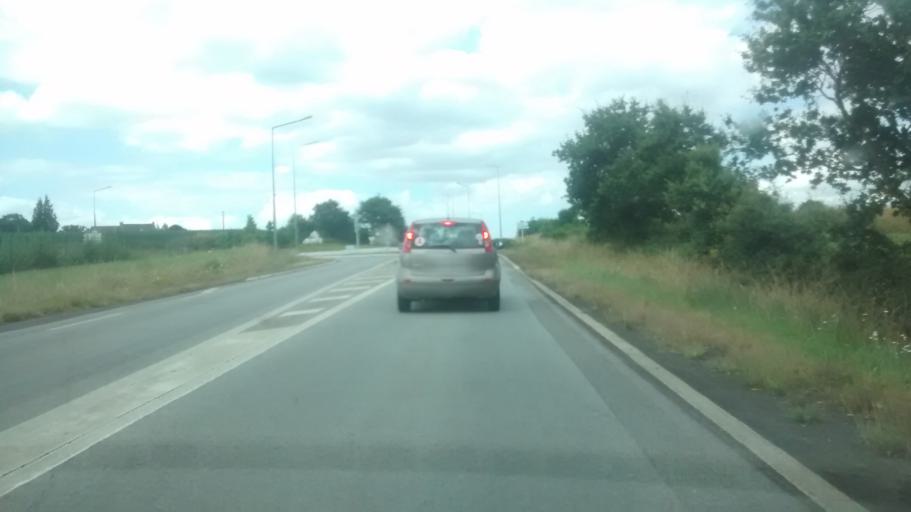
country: FR
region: Brittany
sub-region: Departement du Morbihan
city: Mauron
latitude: 48.0945
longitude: -2.2683
